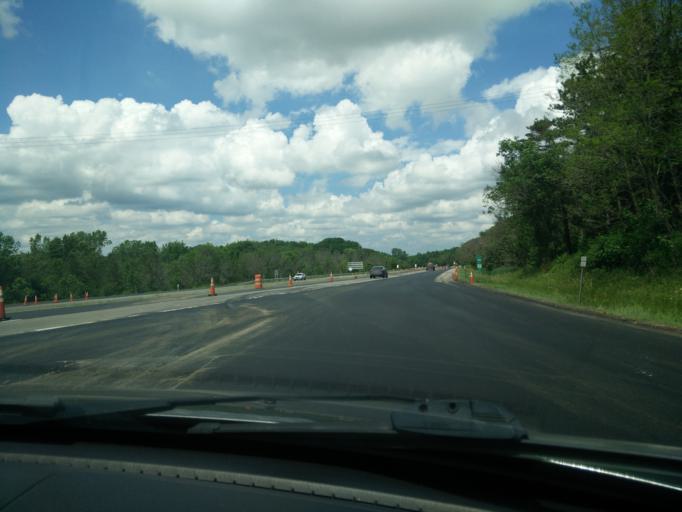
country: US
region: New York
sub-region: Erie County
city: East Aurora
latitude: 42.7698
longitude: -78.5923
